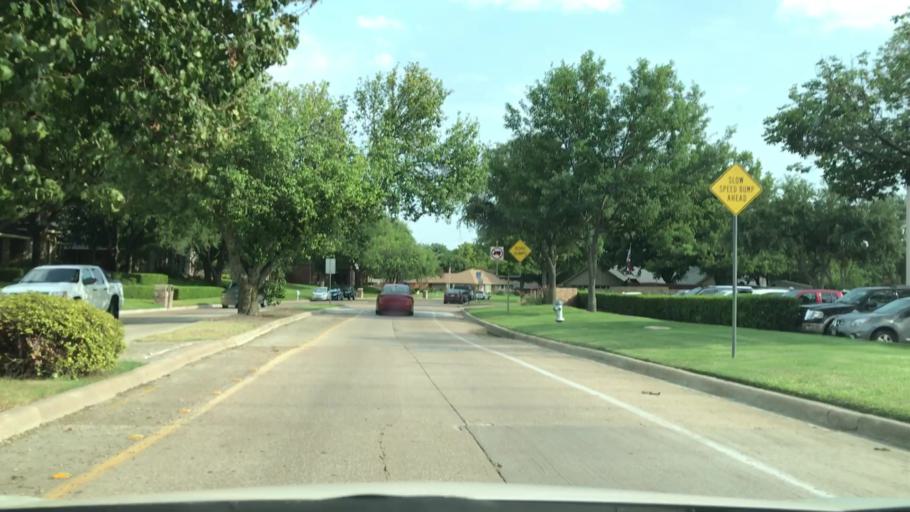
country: US
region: Texas
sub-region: Rockwall County
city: Rockwall
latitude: 32.9291
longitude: -96.4688
